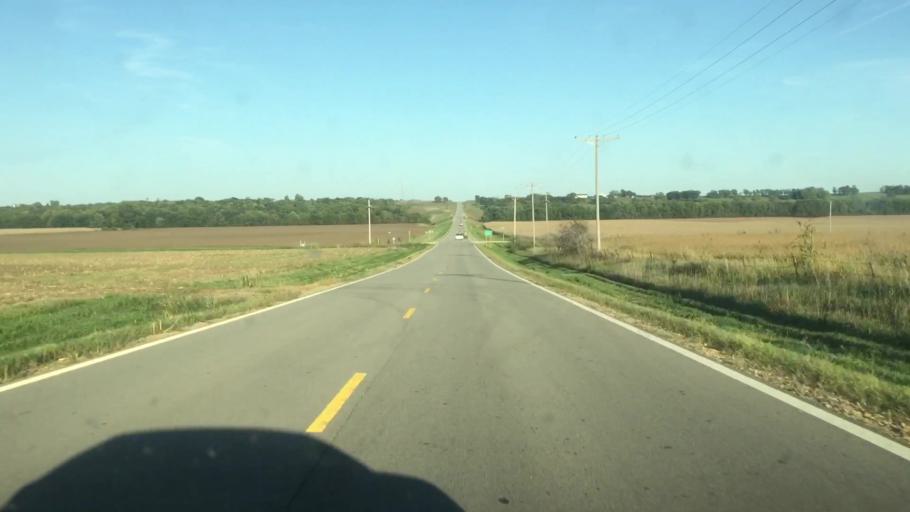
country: US
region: Kansas
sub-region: Brown County
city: Horton
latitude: 39.5875
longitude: -95.5663
